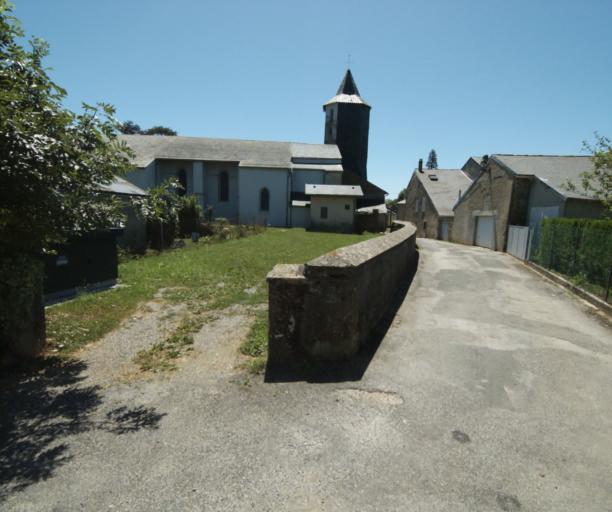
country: FR
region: Midi-Pyrenees
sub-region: Departement du Tarn
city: Dourgne
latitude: 43.4307
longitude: 2.1673
